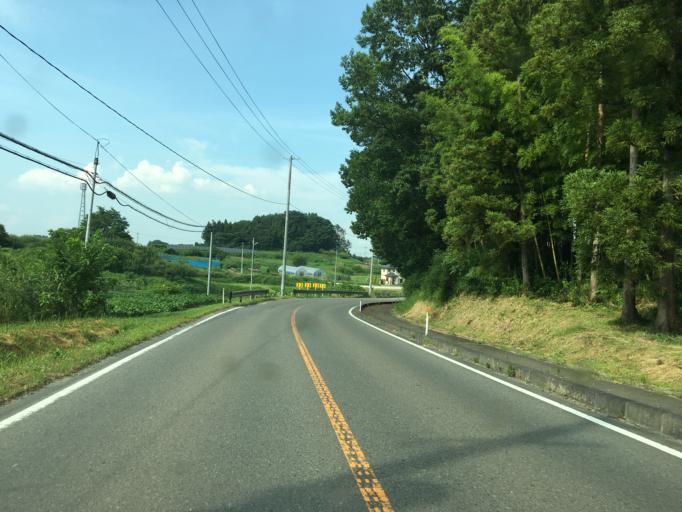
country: JP
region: Fukushima
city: Koriyama
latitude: 37.3545
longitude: 140.4148
